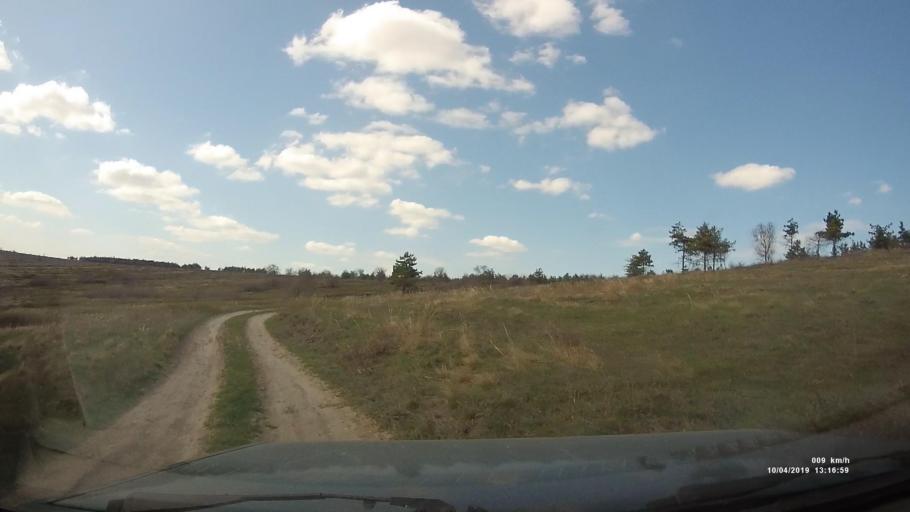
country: RU
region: Rostov
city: Masalovka
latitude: 48.4218
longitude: 40.2553
